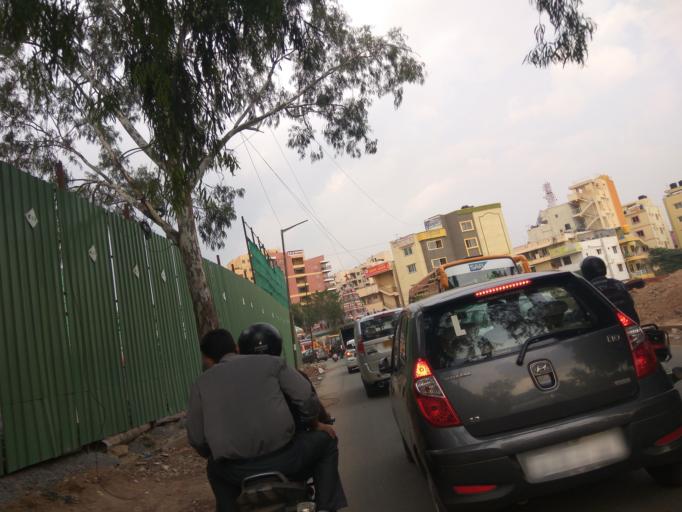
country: IN
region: Karnataka
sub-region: Bangalore Urban
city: Bangalore
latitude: 12.9723
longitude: 77.7110
